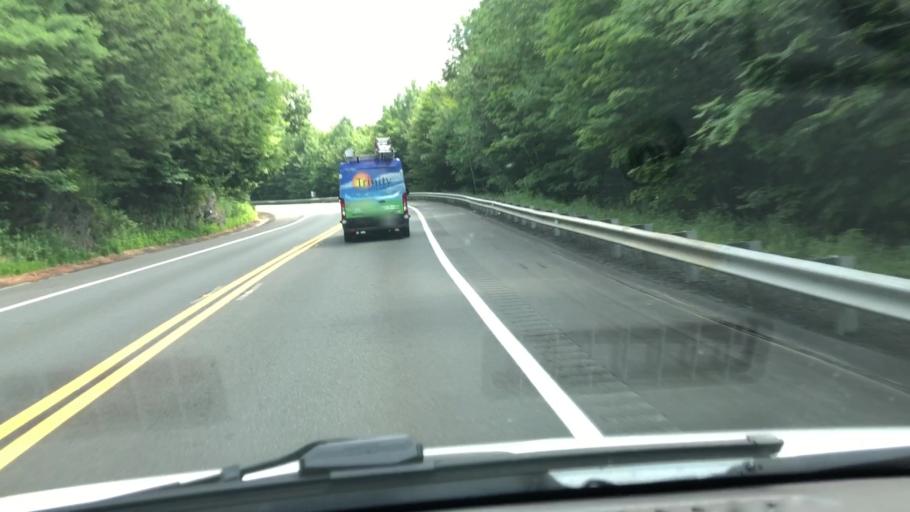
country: US
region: Massachusetts
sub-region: Hampshire County
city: Chesterfield
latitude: 42.4516
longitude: -72.8222
